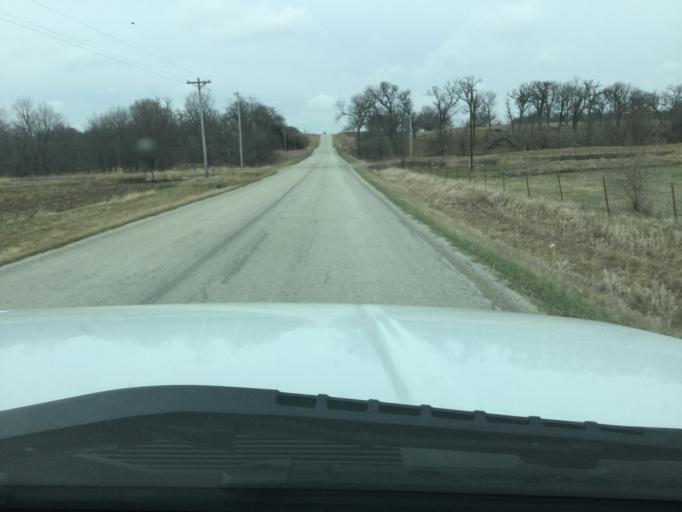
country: US
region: Kansas
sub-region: Nemaha County
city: Sabetha
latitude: 39.8566
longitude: -95.7142
